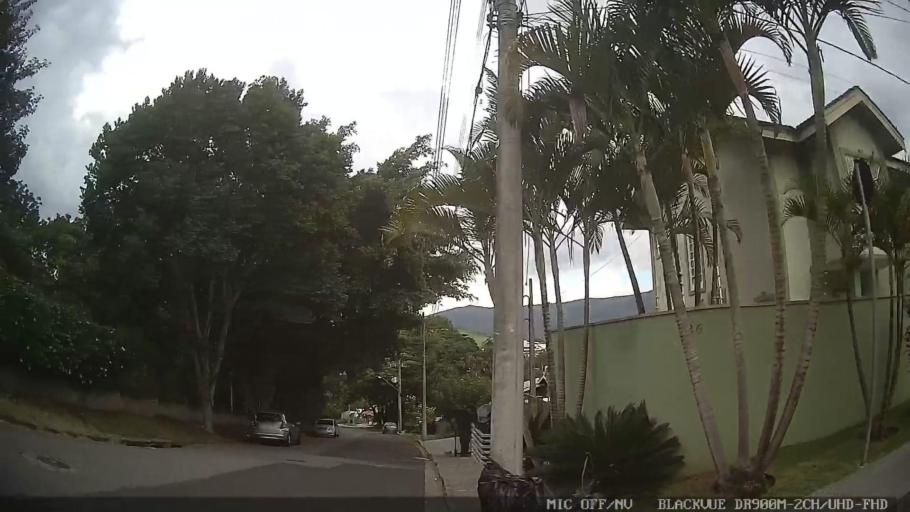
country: BR
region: Sao Paulo
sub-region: Atibaia
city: Atibaia
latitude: -23.1332
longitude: -46.5593
